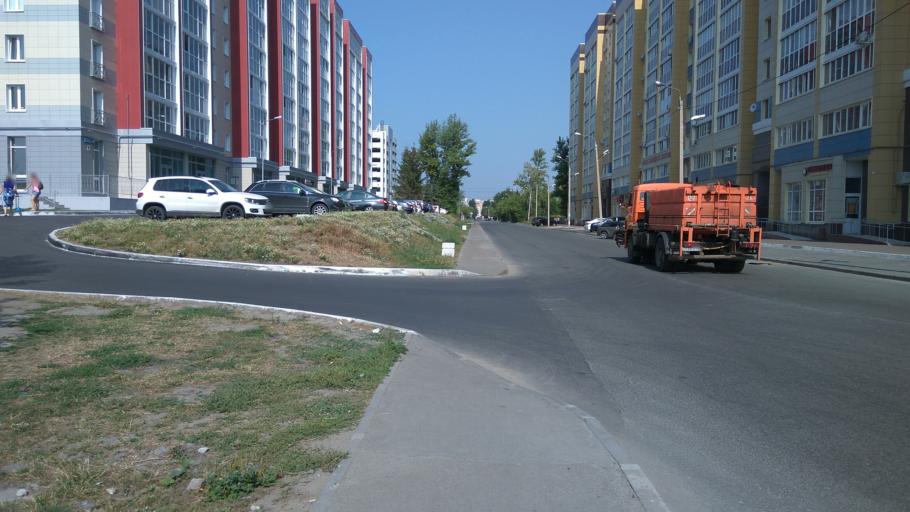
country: RU
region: Tatarstan
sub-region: Gorod Kazan'
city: Kazan
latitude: 55.7685
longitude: 49.1538
